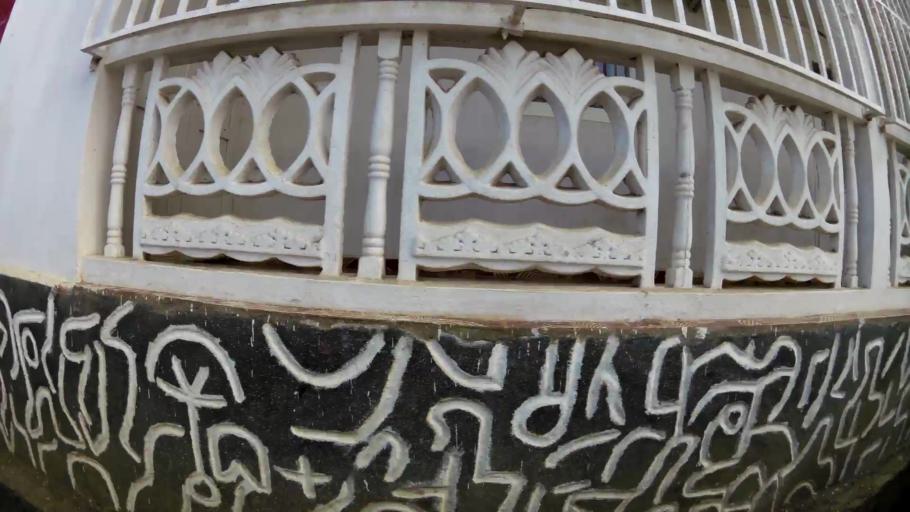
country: YT
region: Mamoudzou
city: Mamoudzou
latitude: -12.7814
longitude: 45.2215
